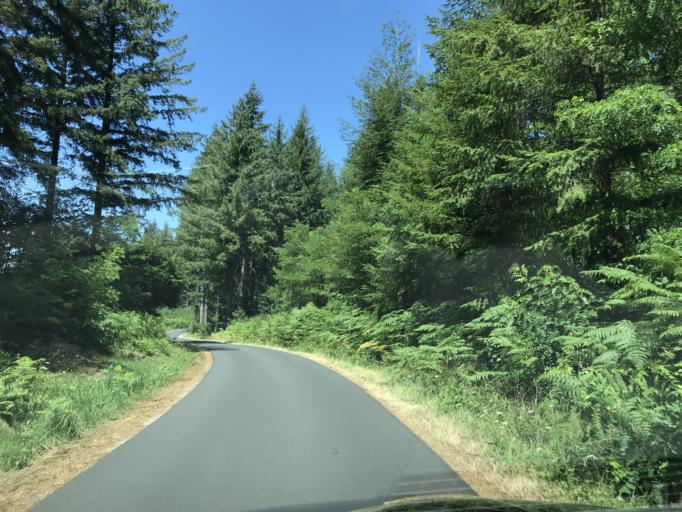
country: FR
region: Limousin
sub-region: Departement de la Correze
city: Neuvic
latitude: 45.3778
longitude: 2.2330
